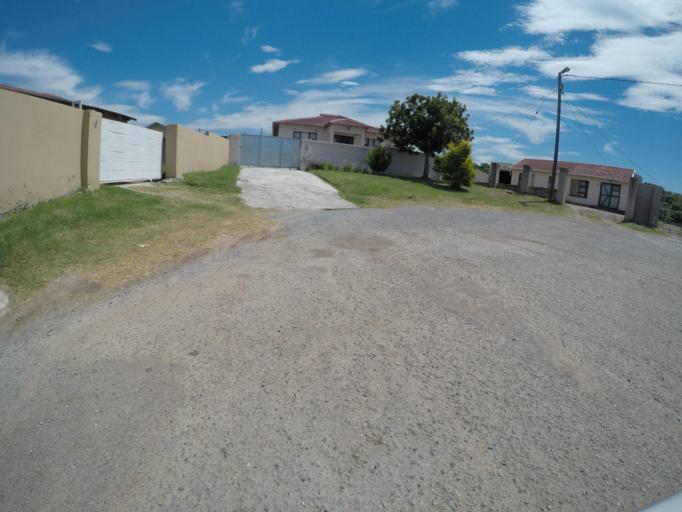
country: ZA
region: Eastern Cape
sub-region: Buffalo City Metropolitan Municipality
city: East London
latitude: -33.0432
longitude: 27.8677
